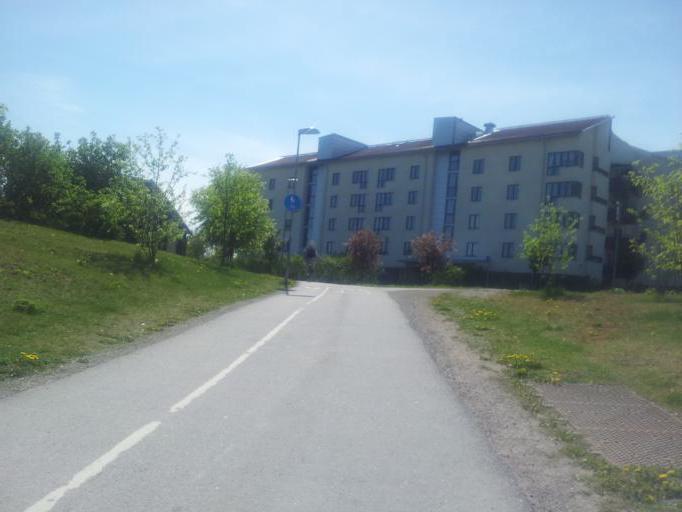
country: SE
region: Uppsala
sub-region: Uppsala Kommun
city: Uppsala
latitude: 59.8751
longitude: 17.6752
